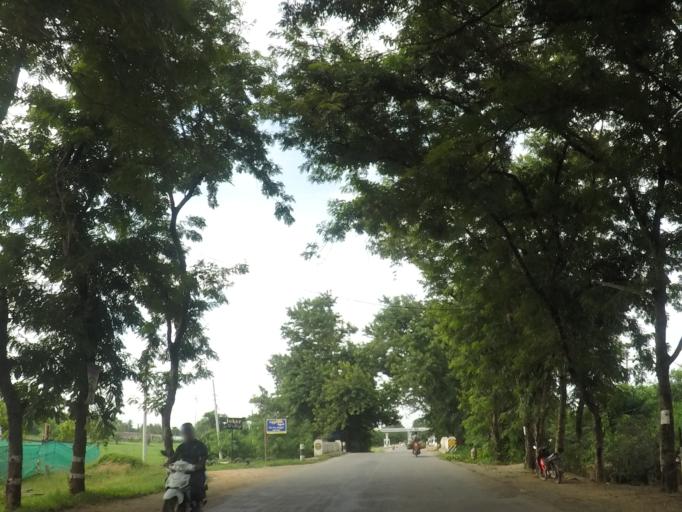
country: MM
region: Bago
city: Pyay
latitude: 18.8320
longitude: 95.2715
